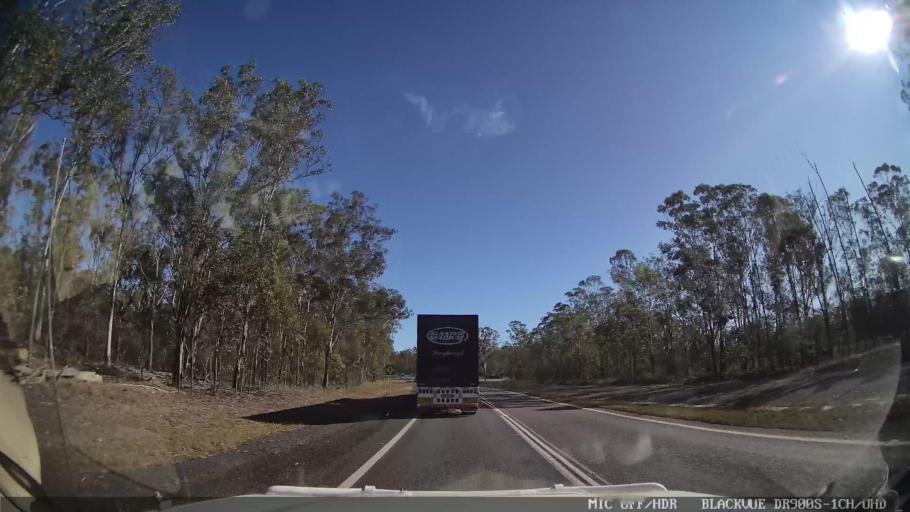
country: AU
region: Queensland
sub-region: Bundaberg
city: Childers
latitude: -25.2107
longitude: 152.0846
